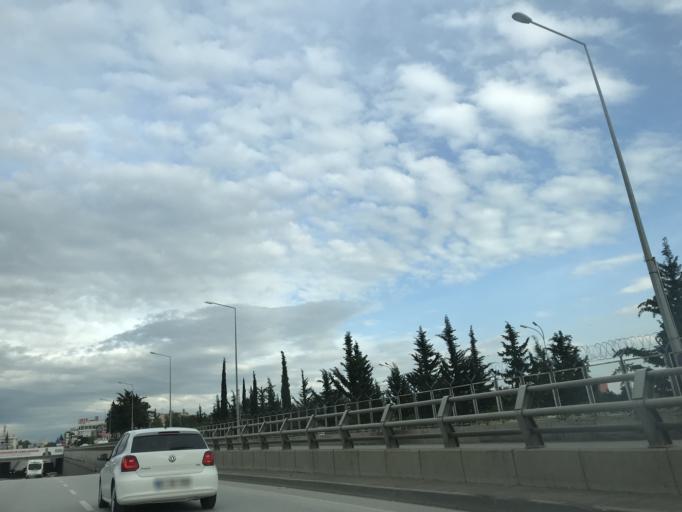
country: TR
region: Adana
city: Seyhan
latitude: 36.9935
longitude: 35.2970
